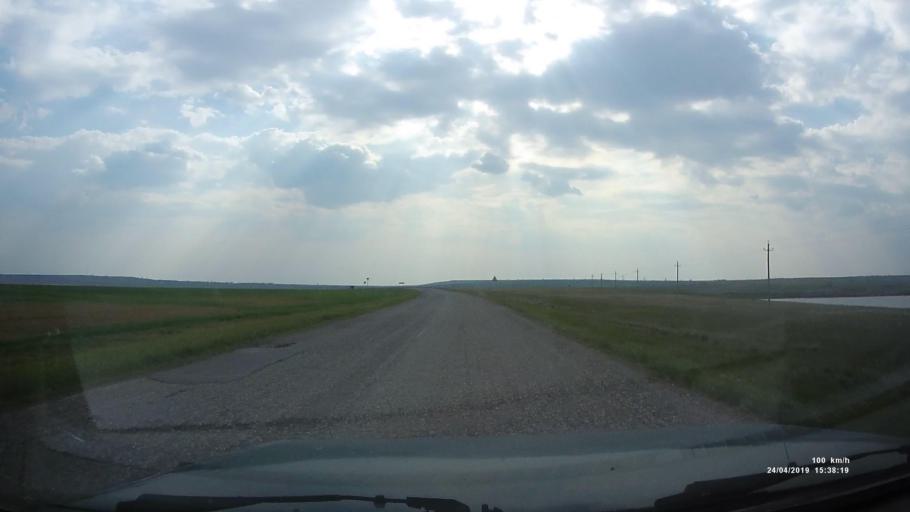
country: RU
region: Kalmykiya
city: Yashalta
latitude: 46.5988
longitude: 42.8299
